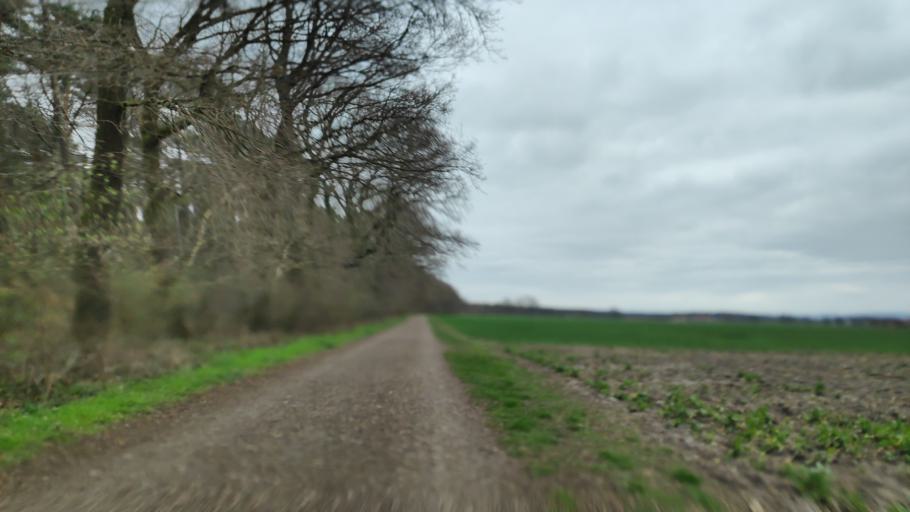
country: DE
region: North Rhine-Westphalia
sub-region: Regierungsbezirk Detmold
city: Petershagen
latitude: 52.3591
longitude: 8.9193
